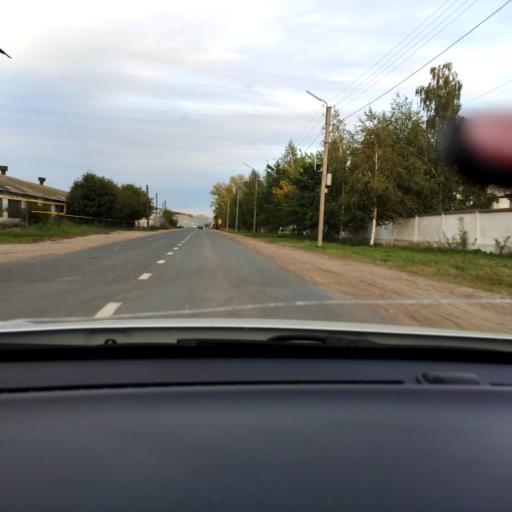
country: RU
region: Tatarstan
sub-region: Zelenodol'skiy Rayon
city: Zelenodolsk
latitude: 55.8387
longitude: 48.5363
